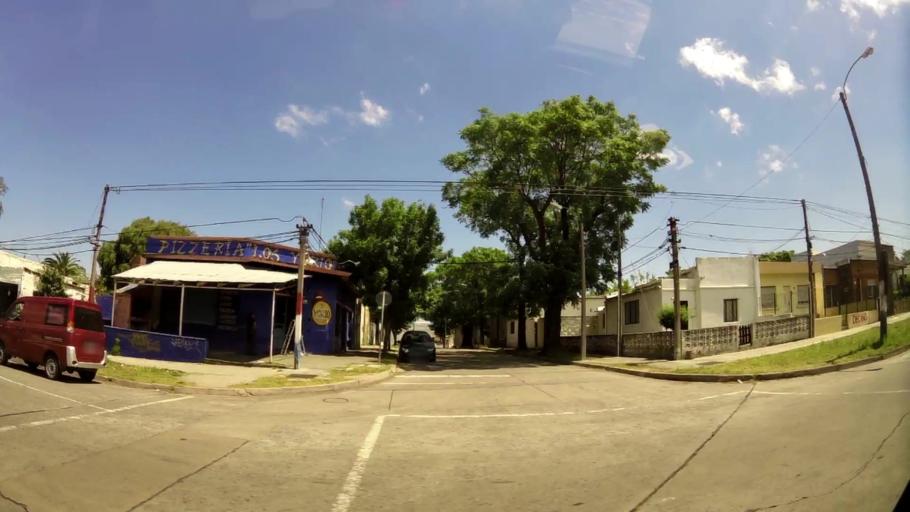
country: UY
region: Montevideo
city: Montevideo
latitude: -34.8608
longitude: -56.2214
